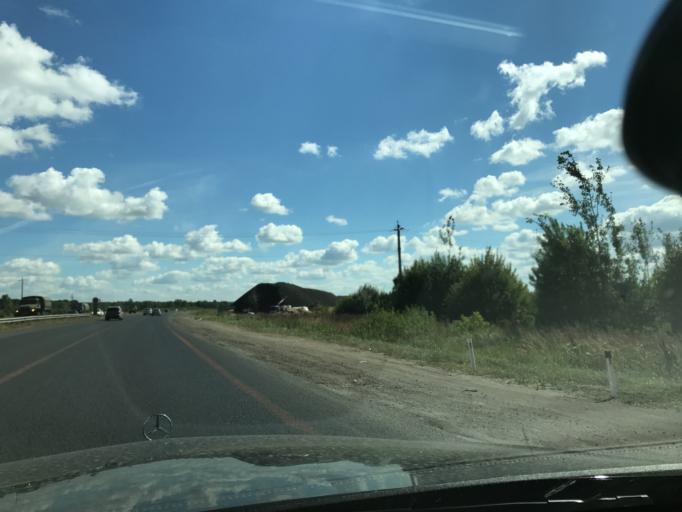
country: RU
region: Nizjnij Novgorod
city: Gorbatovka
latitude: 56.2364
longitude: 43.7366
